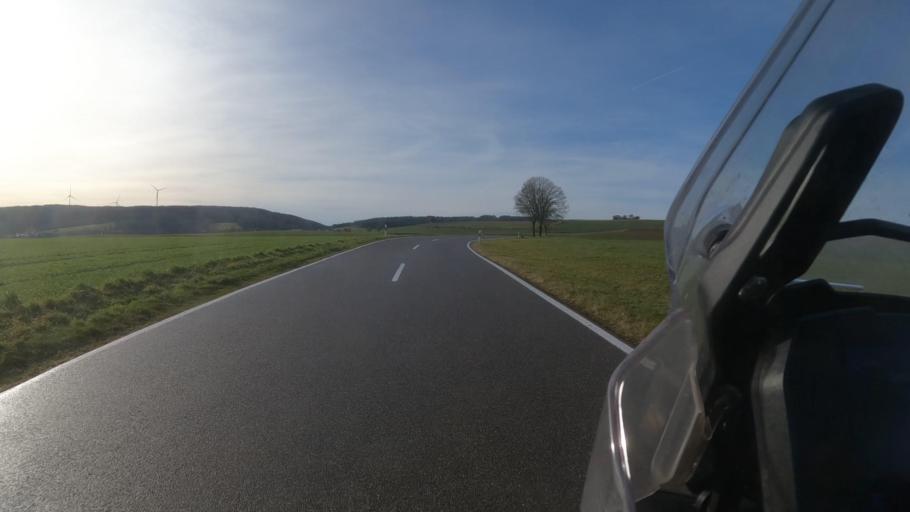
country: DE
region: Baden-Wuerttemberg
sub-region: Freiburg Region
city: Tengen
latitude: 47.7967
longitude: 8.6437
